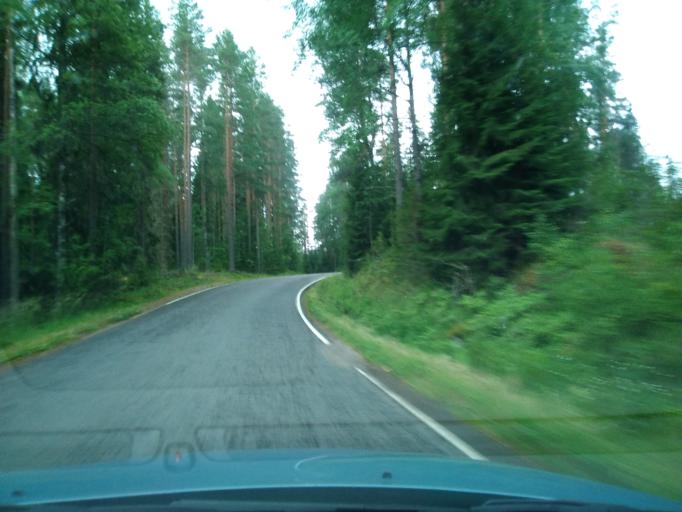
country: FI
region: Uusimaa
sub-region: Helsinki
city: Kaerkoelae
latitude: 60.7883
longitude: 24.0805
